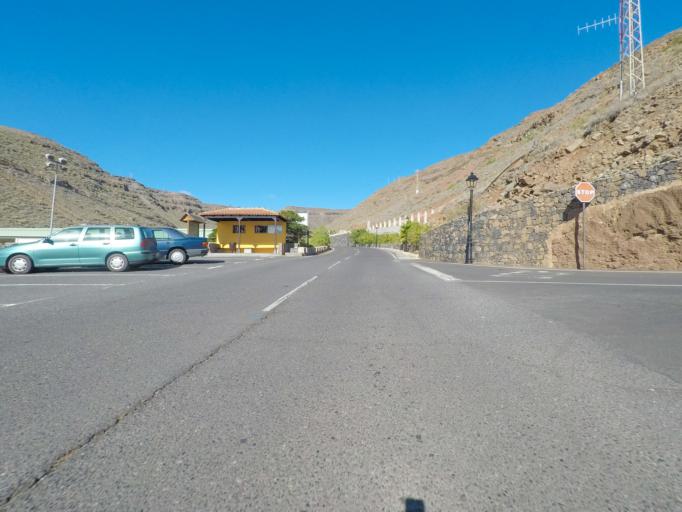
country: ES
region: Canary Islands
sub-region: Provincia de Santa Cruz de Tenerife
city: Alajero
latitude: 28.0323
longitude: -17.1999
